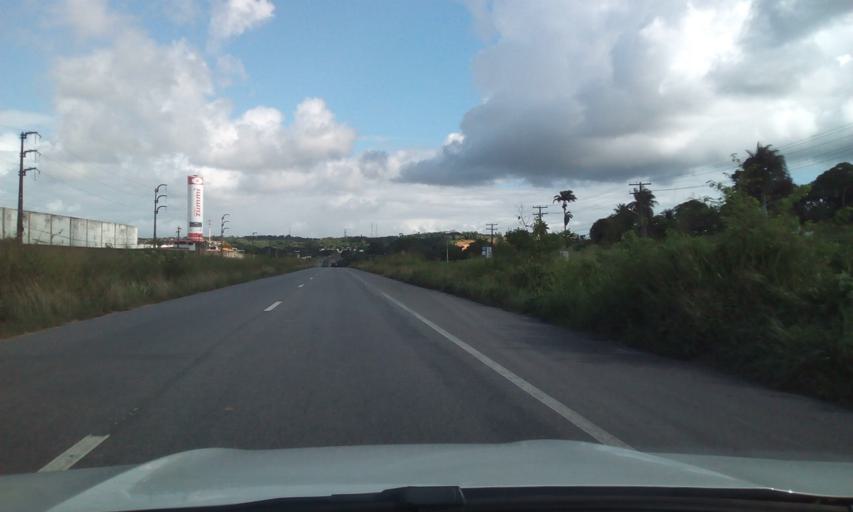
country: BR
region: Pernambuco
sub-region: Abreu E Lima
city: Abreu e Lima
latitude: -7.9379
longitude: -34.9034
